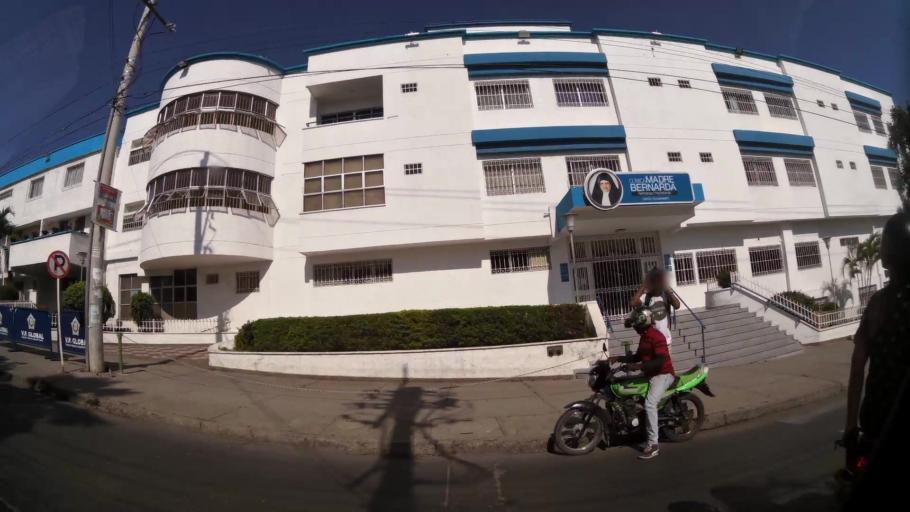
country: CO
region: Bolivar
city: Cartagena
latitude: 10.3943
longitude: -75.4768
